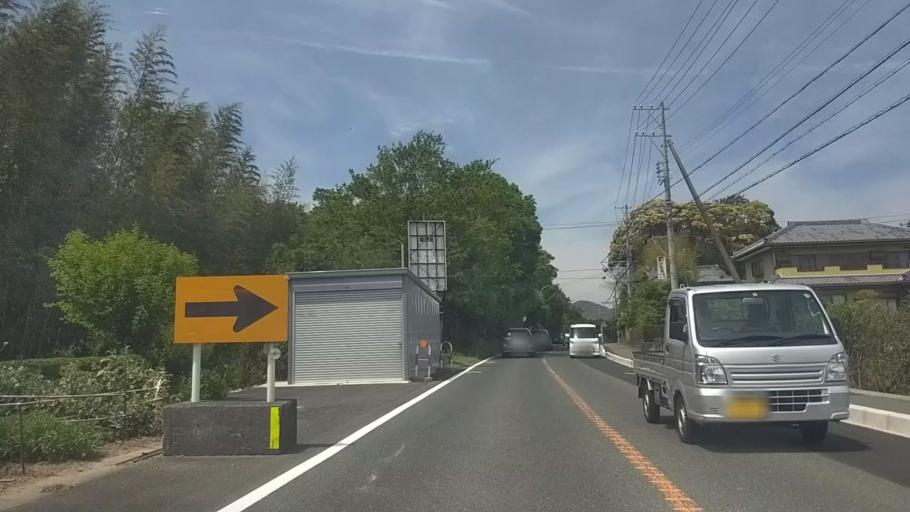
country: JP
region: Shizuoka
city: Kosai-shi
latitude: 34.7437
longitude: 137.5144
